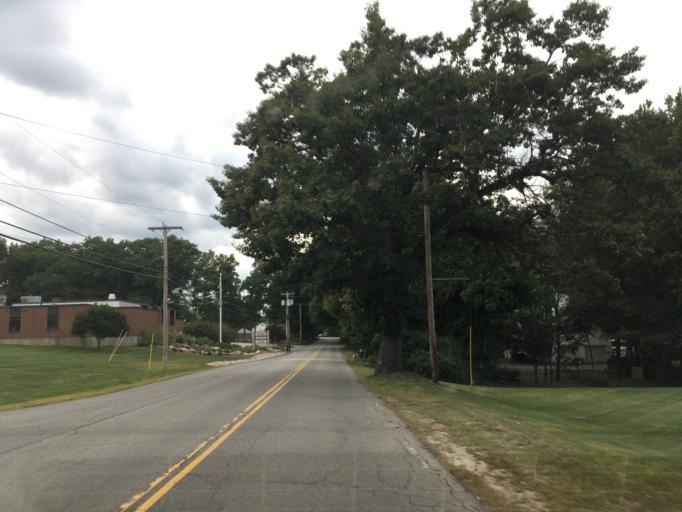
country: US
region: New Hampshire
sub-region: Rockingham County
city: Exeter
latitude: 43.0112
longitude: -70.9143
